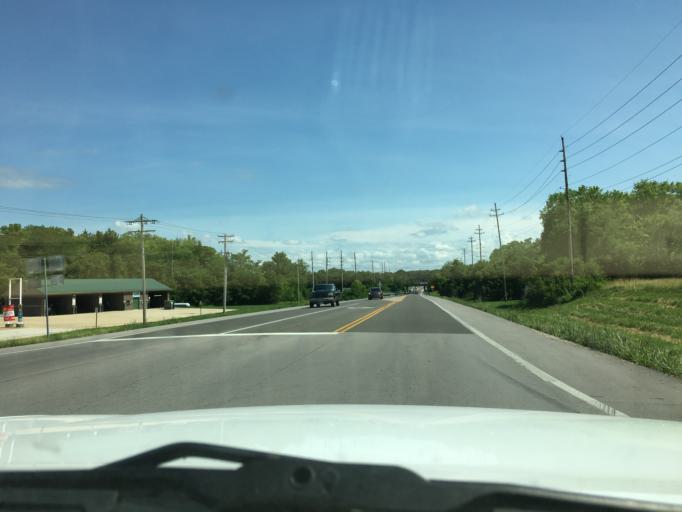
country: US
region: Missouri
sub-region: Franklin County
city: Union
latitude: 38.4547
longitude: -91.0023
